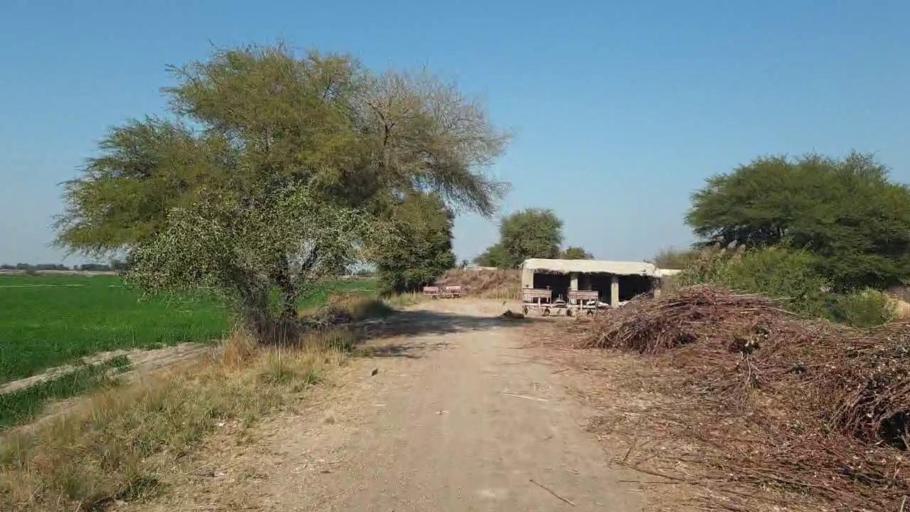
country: PK
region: Sindh
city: Shahdadpur
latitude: 25.9544
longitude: 68.6477
